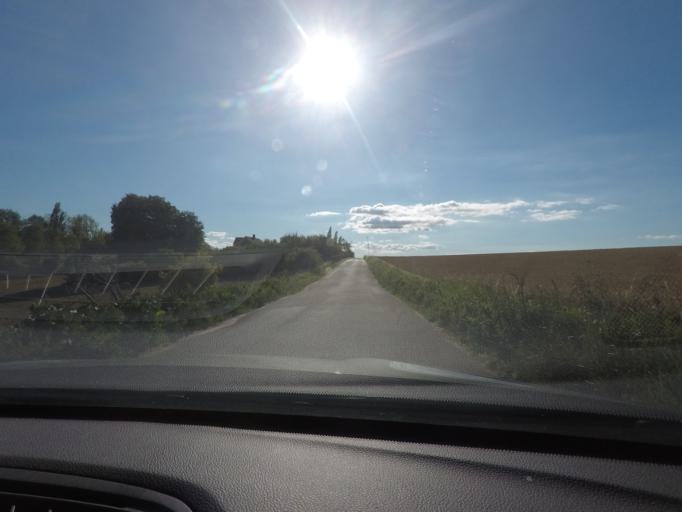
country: DK
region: Zealand
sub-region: Lolland Kommune
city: Maribo
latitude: 54.9785
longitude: 11.5241
